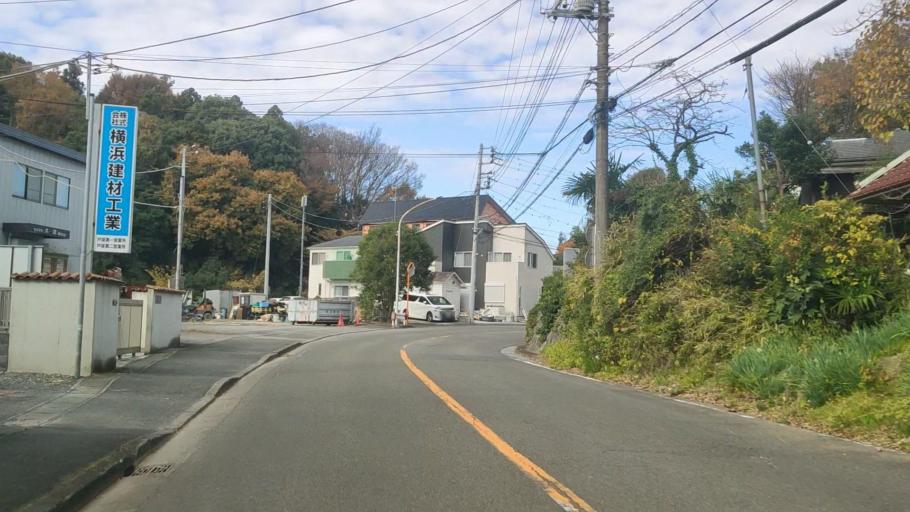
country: JP
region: Kanagawa
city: Yokohama
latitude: 35.4376
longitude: 139.5443
